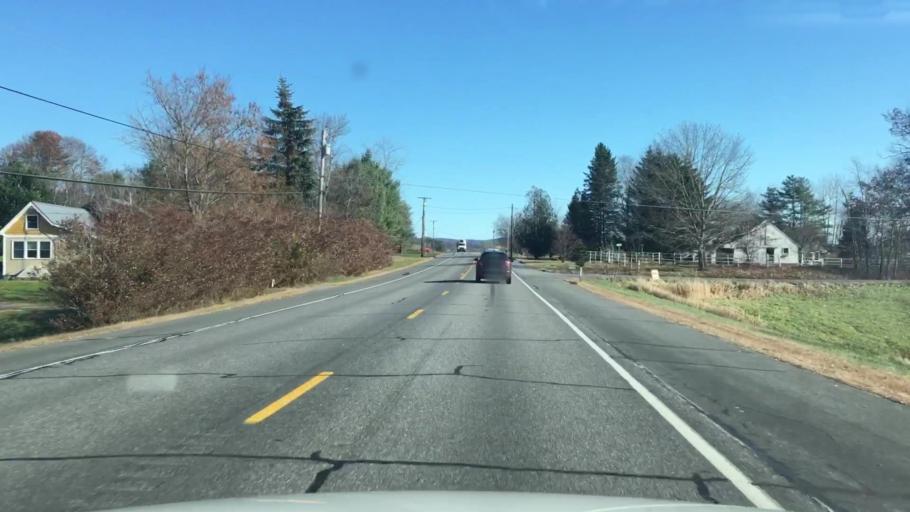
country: US
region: Maine
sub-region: Knox County
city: Union
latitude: 44.2161
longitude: -69.3076
